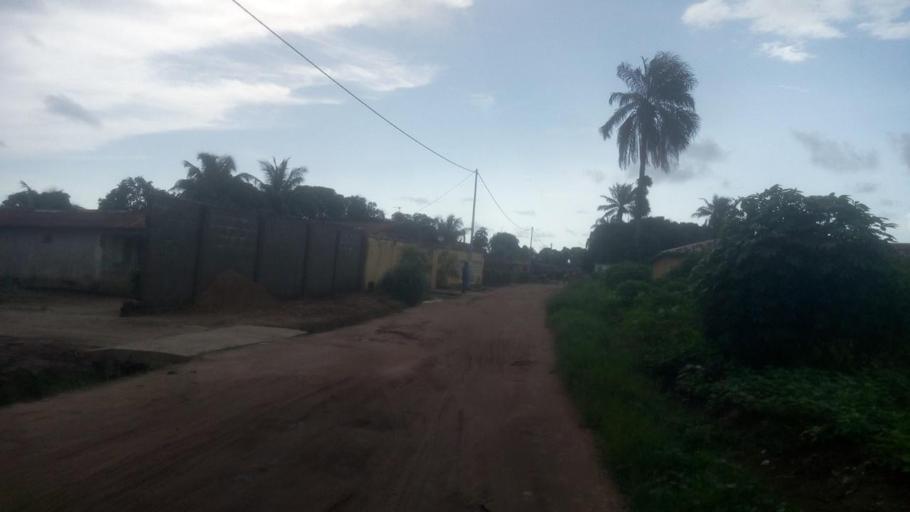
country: SL
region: Northern Province
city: Masoyila
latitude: 8.6063
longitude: -13.1868
